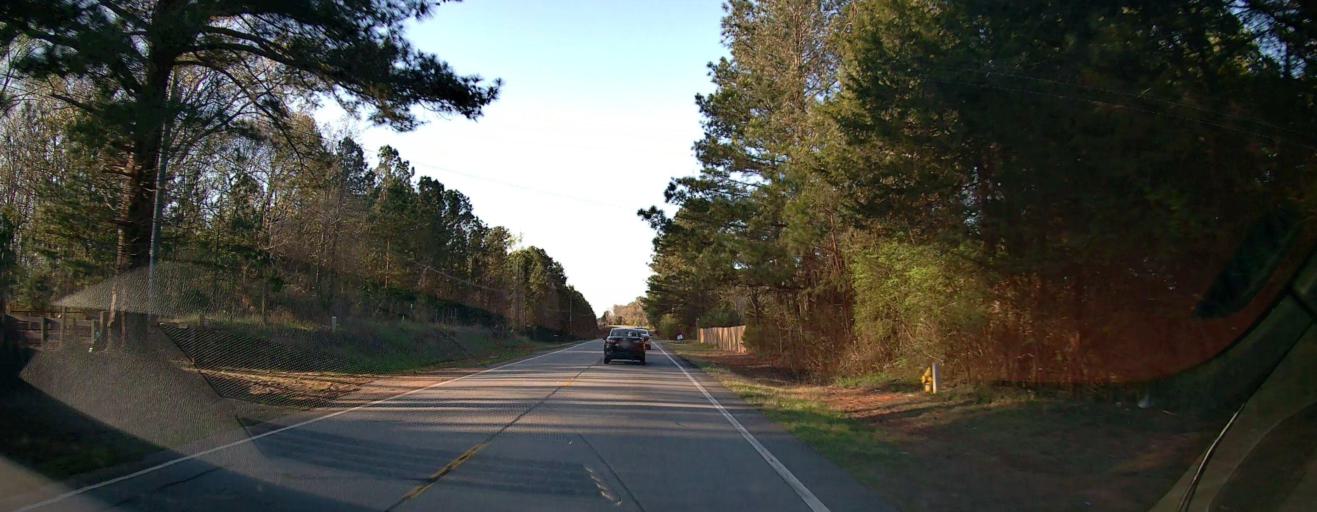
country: US
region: Georgia
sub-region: Newton County
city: Oakwood
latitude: 33.4890
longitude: -83.9170
